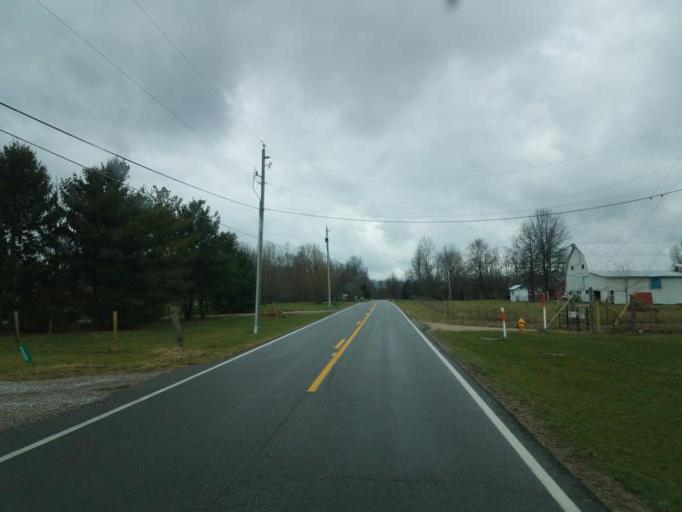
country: US
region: Ohio
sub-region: Delaware County
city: Sunbury
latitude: 40.2024
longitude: -82.9144
